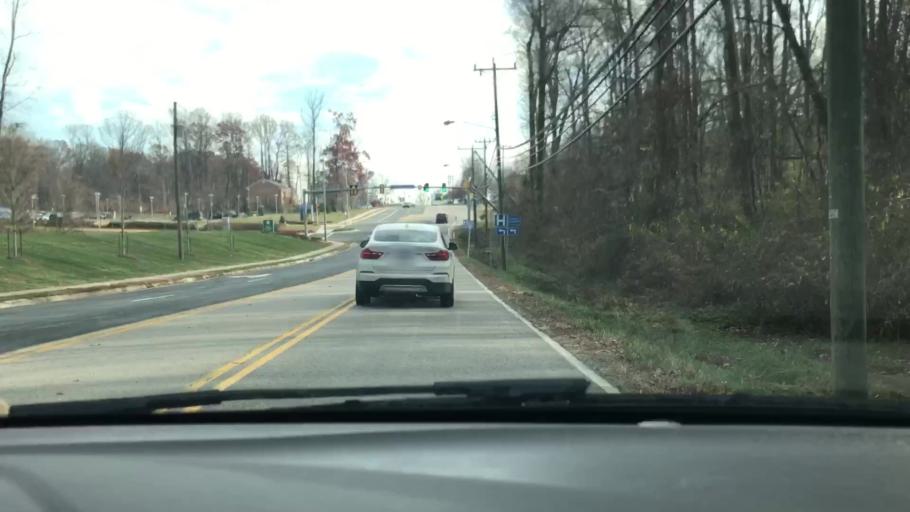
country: US
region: Virginia
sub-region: Fairfax County
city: Merrifield
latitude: 38.8544
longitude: -77.2276
